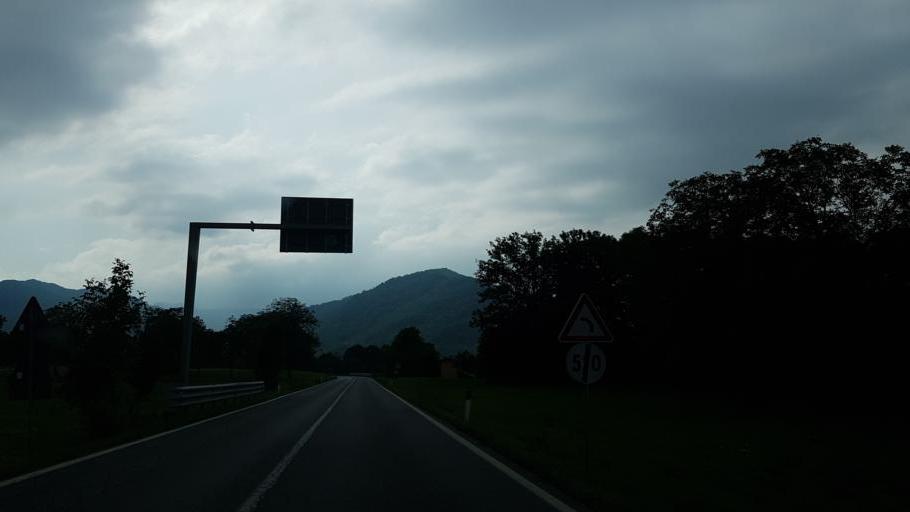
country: IT
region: Piedmont
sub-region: Provincia di Cuneo
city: Roccasparvera
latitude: 44.3349
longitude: 7.4318
